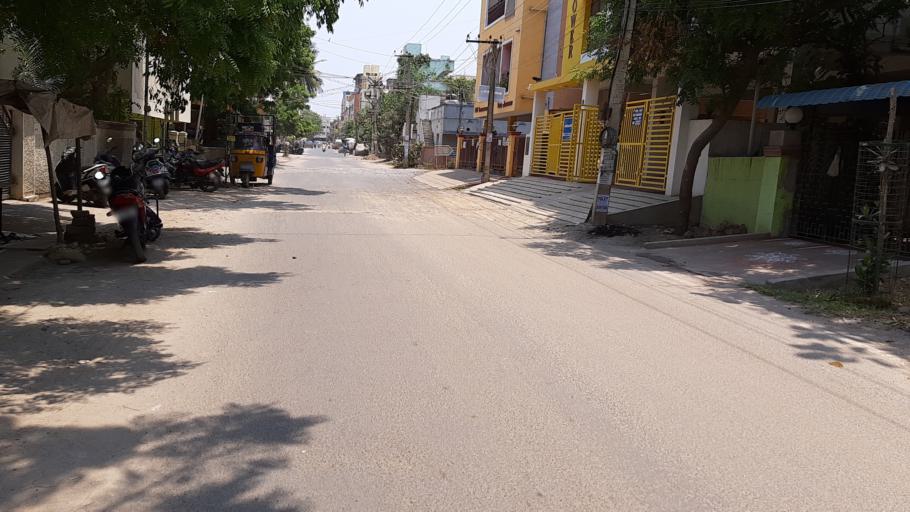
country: IN
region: Tamil Nadu
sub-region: Kancheepuram
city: Manappakkam
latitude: 13.0286
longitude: 80.1869
